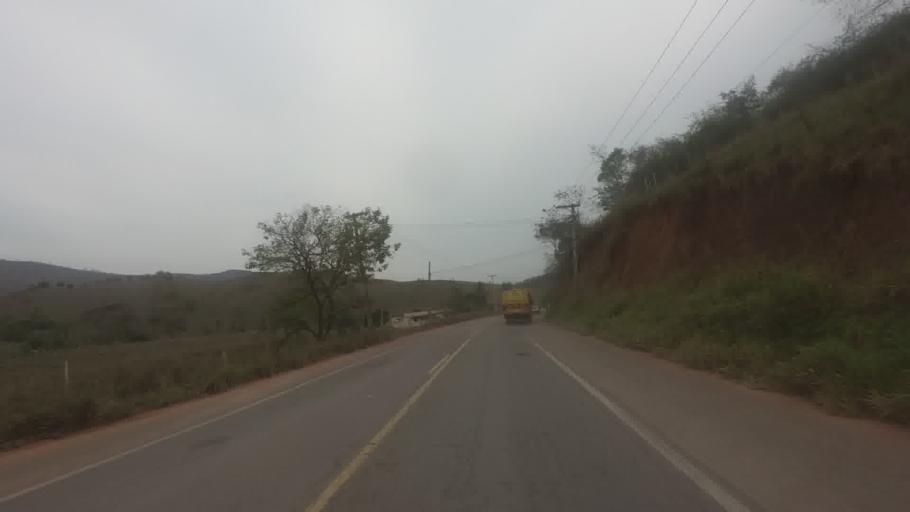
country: BR
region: Rio de Janeiro
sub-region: Santo Antonio De Padua
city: Santo Antonio de Padua
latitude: -21.6162
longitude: -42.2533
